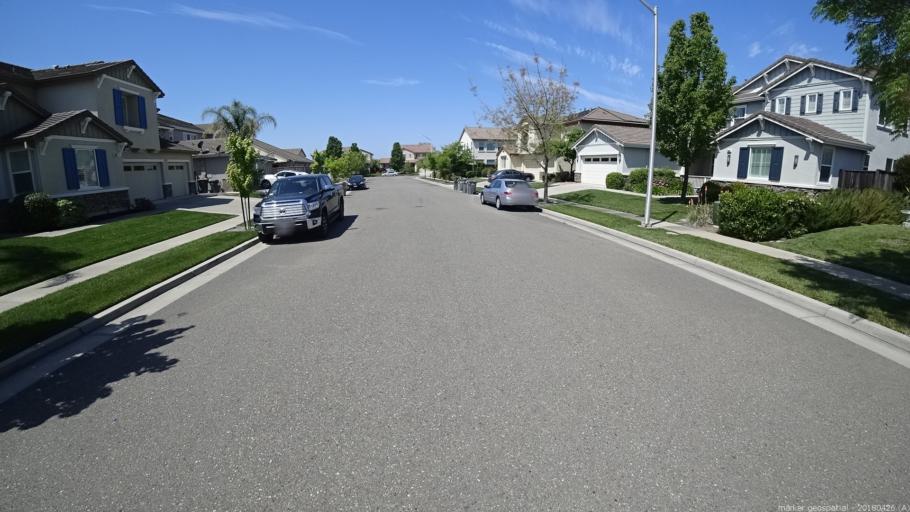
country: US
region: California
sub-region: Yolo County
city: West Sacramento
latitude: 38.5296
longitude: -121.5801
